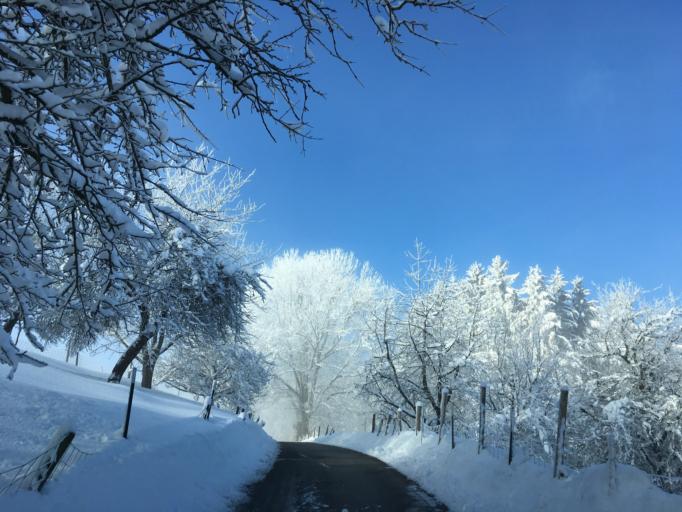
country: DE
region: Bavaria
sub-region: Upper Bavaria
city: Rimsting
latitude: 47.8837
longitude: 12.3144
